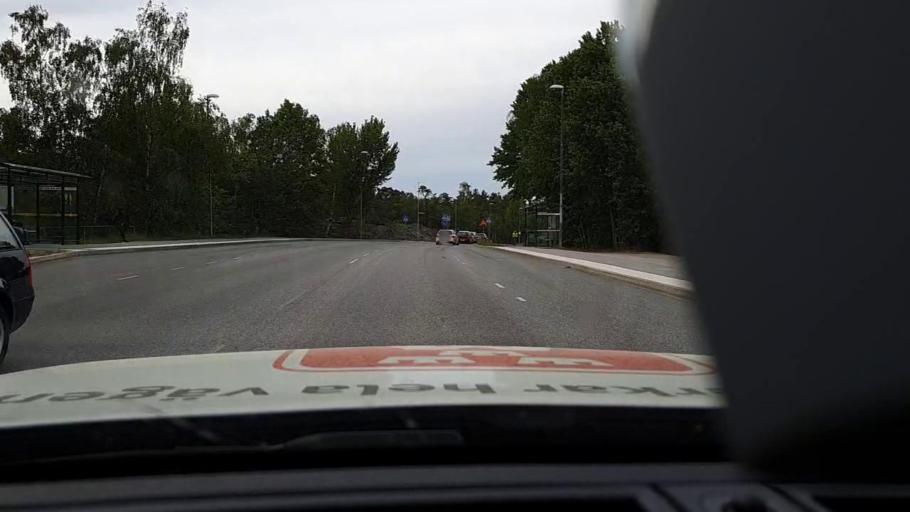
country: SE
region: Stockholm
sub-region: Haninge Kommun
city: Haninge
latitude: 59.1698
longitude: 18.1616
